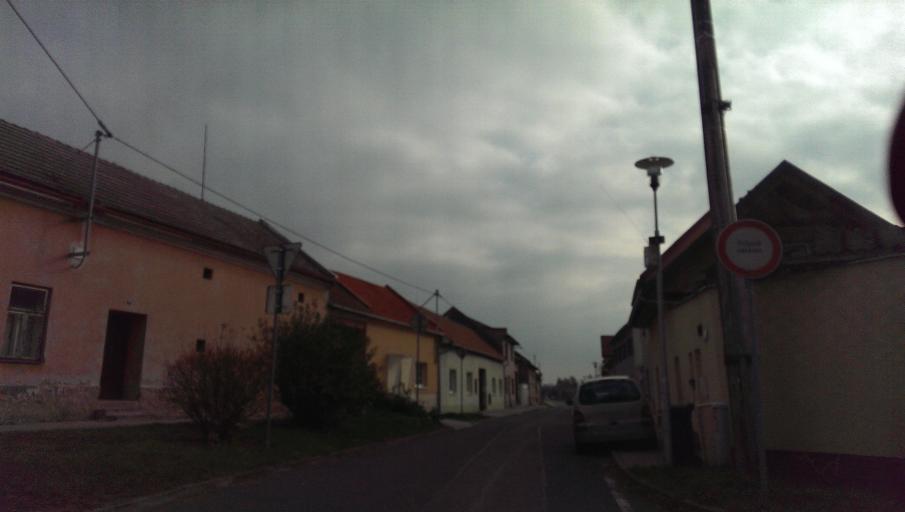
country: CZ
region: Zlin
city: Tlumacov
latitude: 49.2521
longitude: 17.4927
